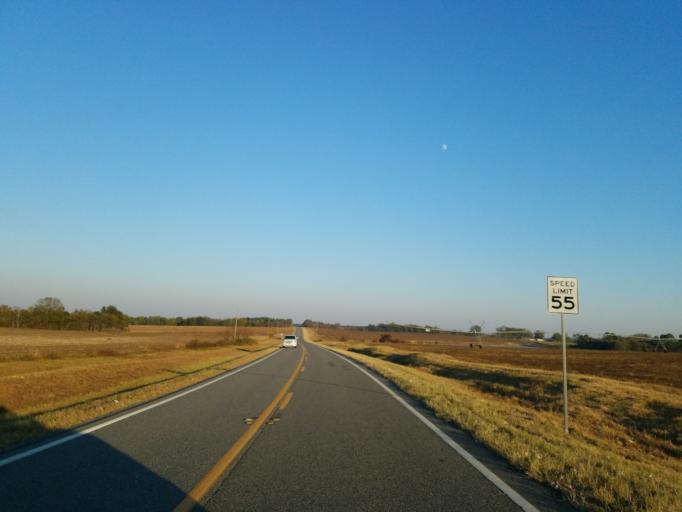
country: US
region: Georgia
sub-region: Wilcox County
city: Rochelle
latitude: 31.8536
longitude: -83.5857
